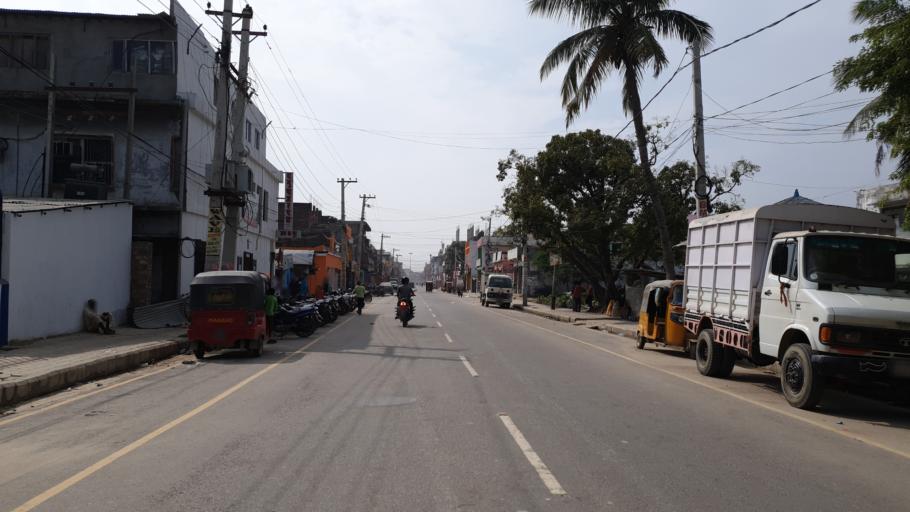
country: NP
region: Central Region
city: Janakpur
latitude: 26.7331
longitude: 85.9352
